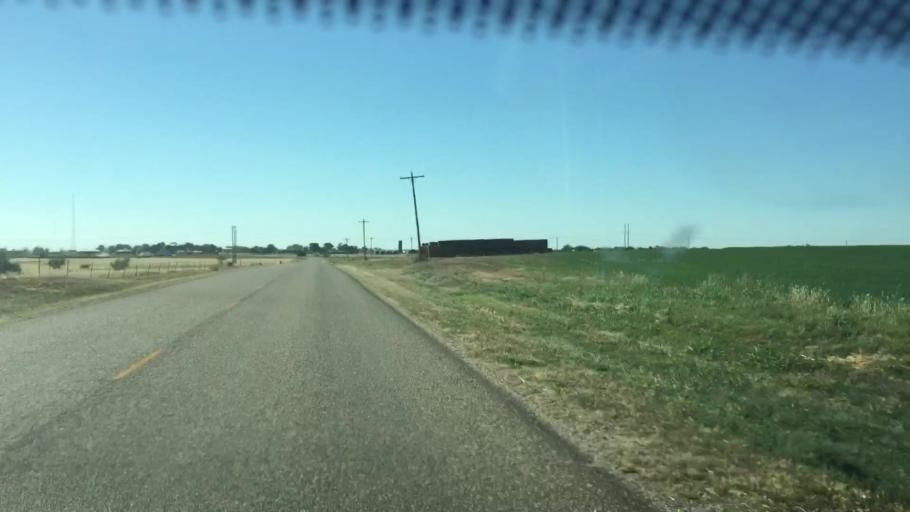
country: US
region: Colorado
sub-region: Prowers County
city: Lamar
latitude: 38.1159
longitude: -102.6016
